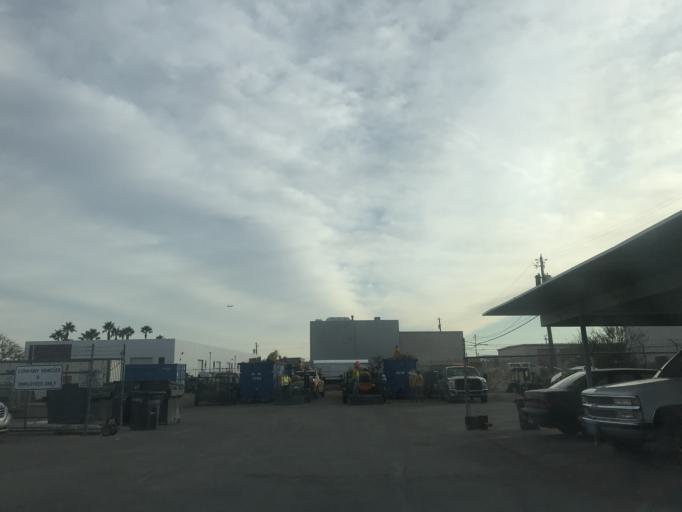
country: US
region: Nevada
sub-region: Clark County
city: Paradise
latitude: 36.1044
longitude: -115.1886
